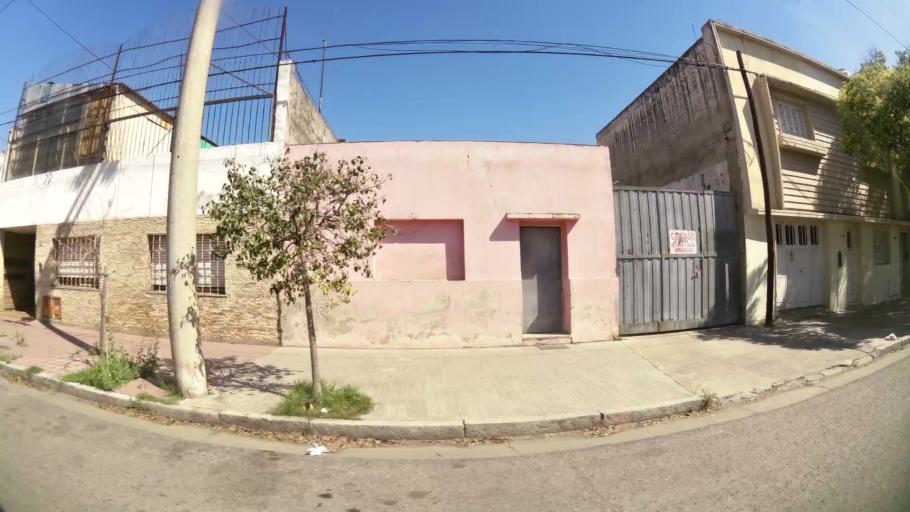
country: AR
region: Cordoba
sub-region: Departamento de Capital
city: Cordoba
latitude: -31.4005
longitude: -64.1677
